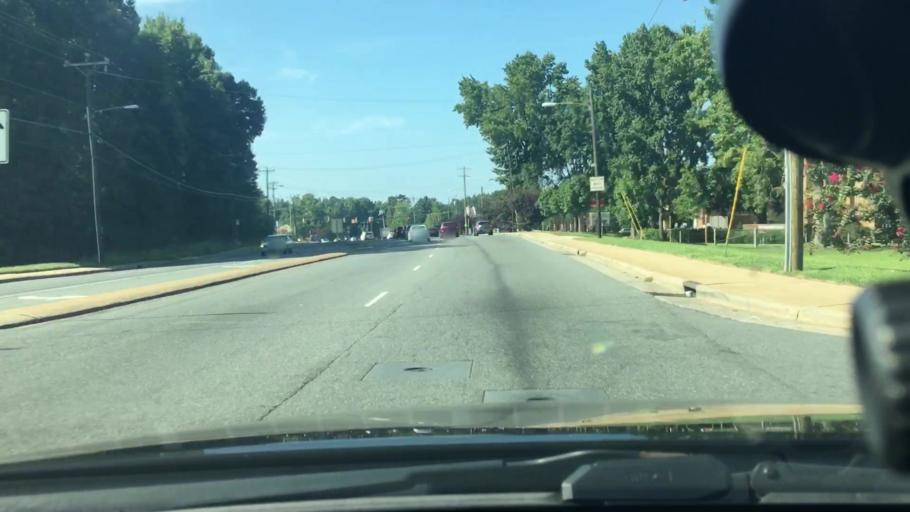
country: US
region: North Carolina
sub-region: Mecklenburg County
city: Matthews
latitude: 35.1878
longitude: -80.7293
